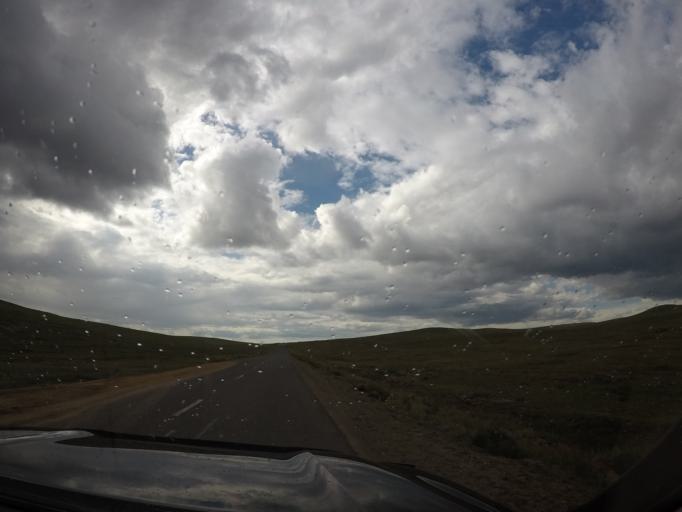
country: MN
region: Hentiy
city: Modot
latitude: 47.5458
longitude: 109.3827
